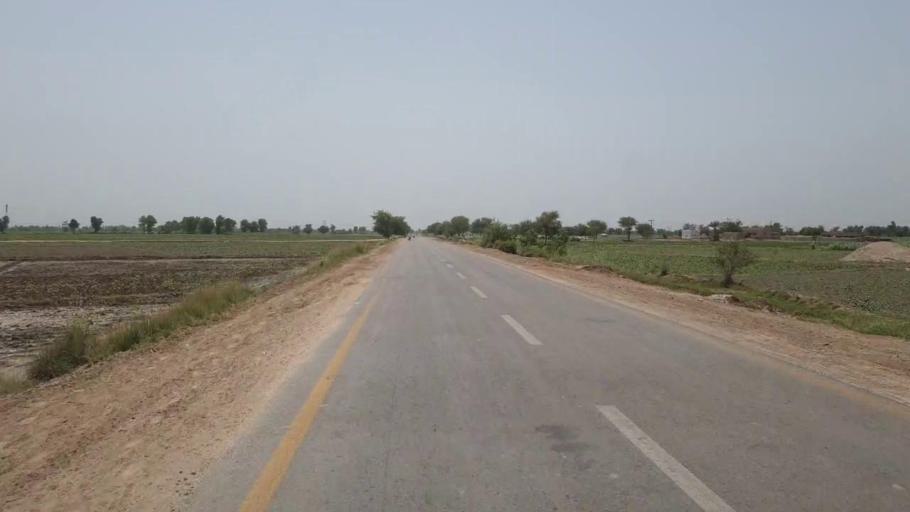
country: PK
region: Sindh
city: Moro
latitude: 26.6059
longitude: 68.0513
